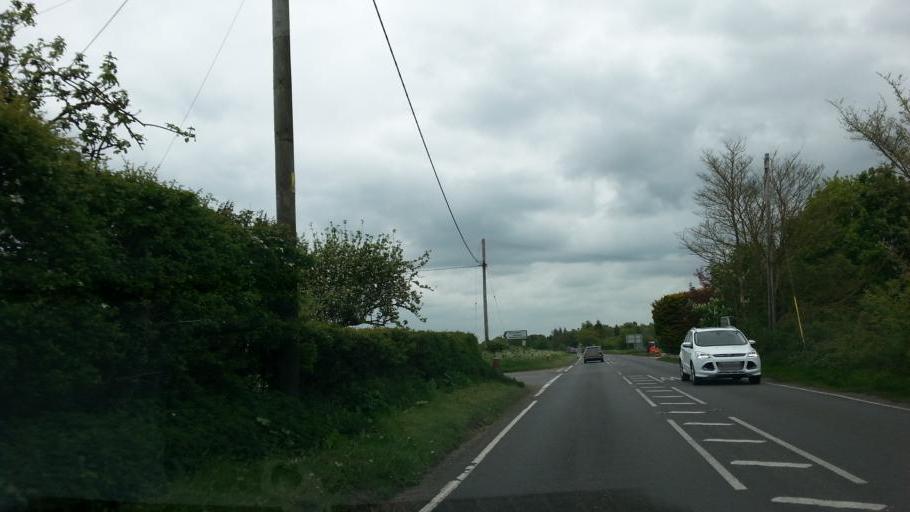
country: GB
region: England
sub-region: Suffolk
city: Lavenham
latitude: 52.1704
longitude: 0.7642
